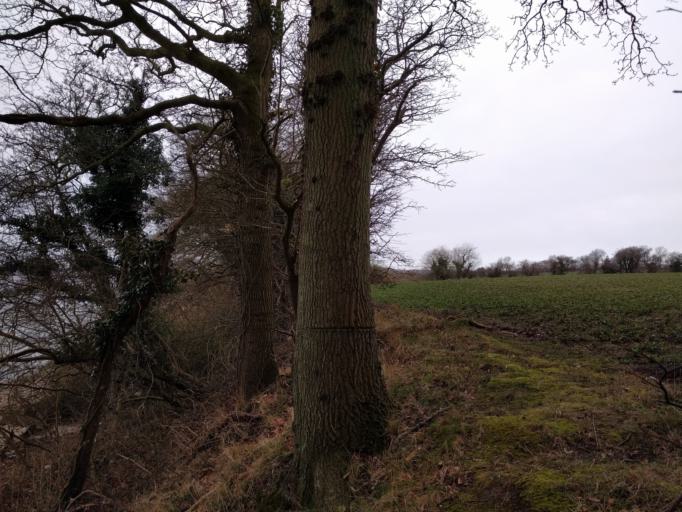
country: DK
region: South Denmark
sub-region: Aabenraa Kommune
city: Lojt Kirkeby
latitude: 55.1269
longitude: 9.5091
